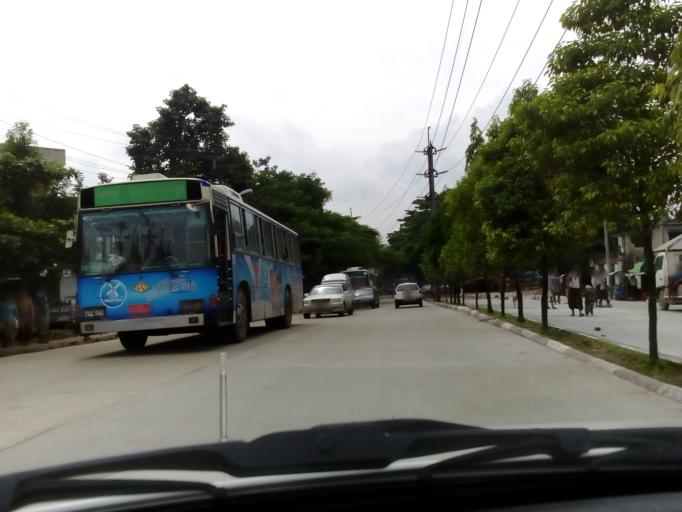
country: MM
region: Yangon
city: Yangon
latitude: 16.8670
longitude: 96.1380
